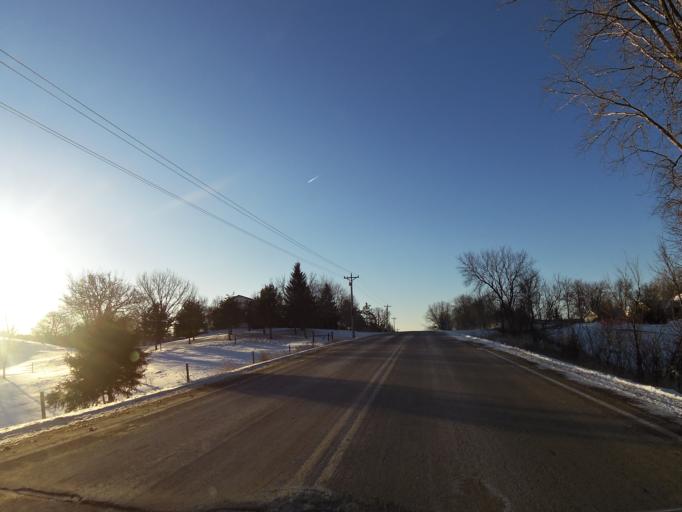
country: US
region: Minnesota
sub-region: Scott County
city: Prior Lake
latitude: 44.6628
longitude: -93.4602
